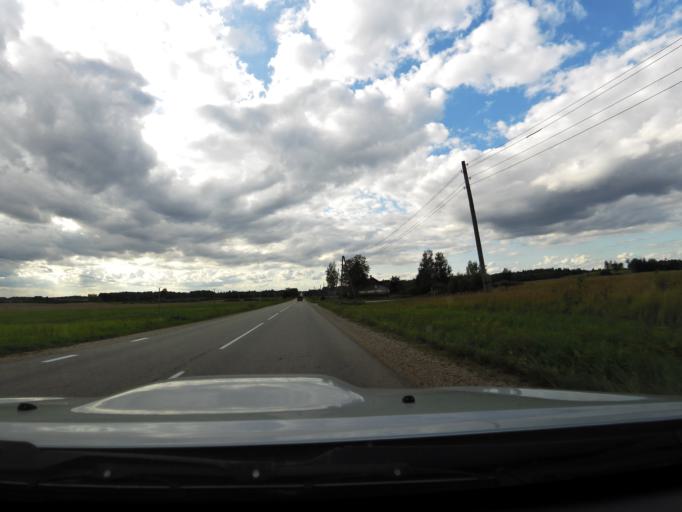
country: LV
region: Ilukste
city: Ilukste
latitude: 55.9635
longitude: 26.0480
